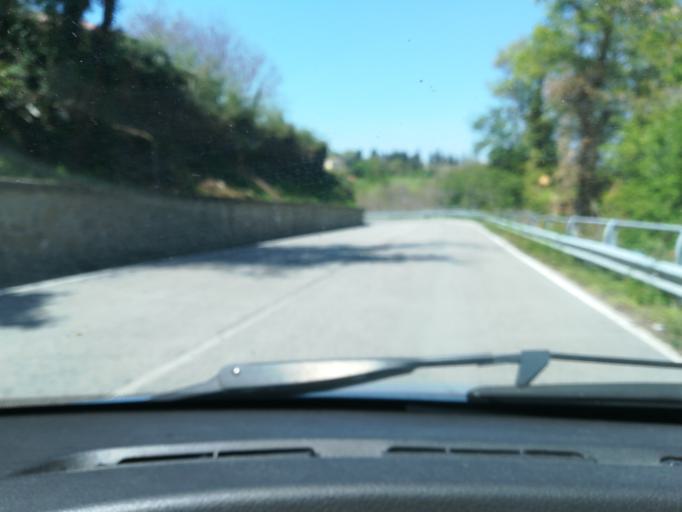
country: IT
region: The Marches
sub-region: Provincia di Macerata
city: Cingoli
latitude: 43.3794
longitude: 13.2149
